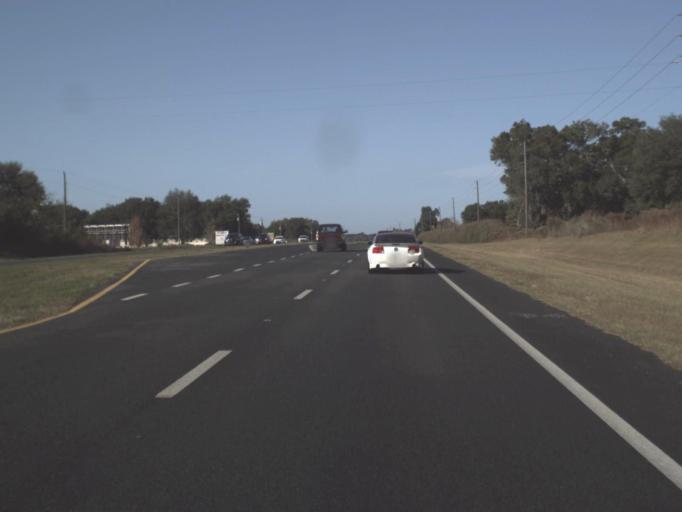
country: US
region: Florida
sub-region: Marion County
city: Belleview
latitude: 29.0259
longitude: -82.1304
